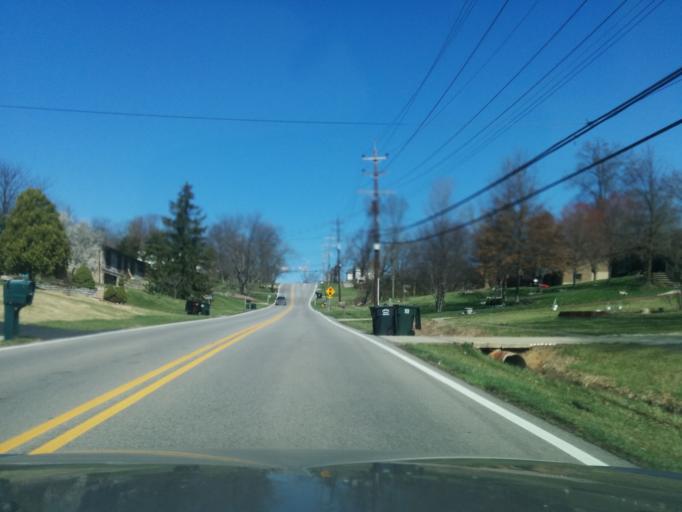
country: US
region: Ohio
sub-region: Hamilton County
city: Dent
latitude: 39.1924
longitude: -84.6275
